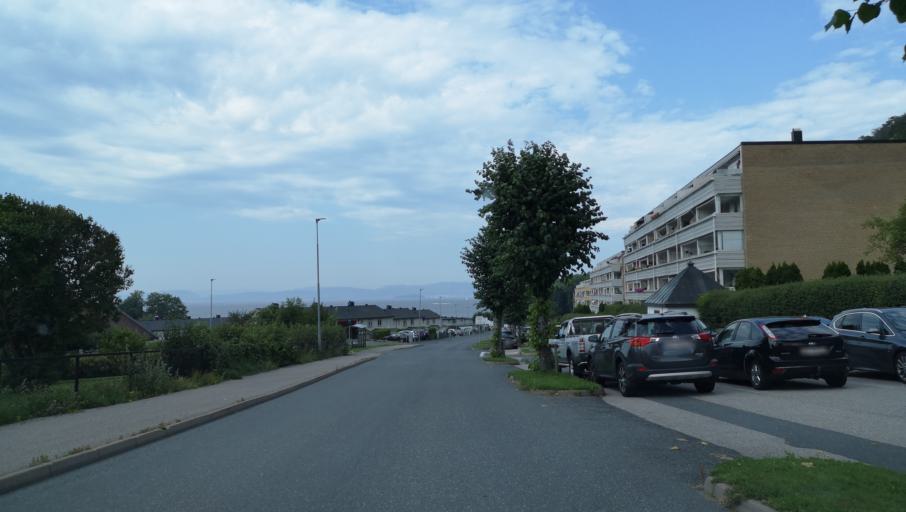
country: NO
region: Ostfold
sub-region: Moss
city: Moss
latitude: 59.4442
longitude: 10.6185
